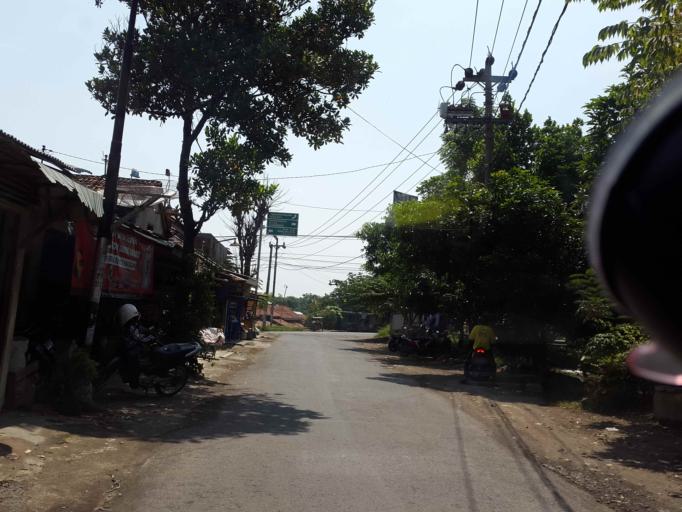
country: ID
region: Central Java
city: Pemalang
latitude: -6.9417
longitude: 109.3895
